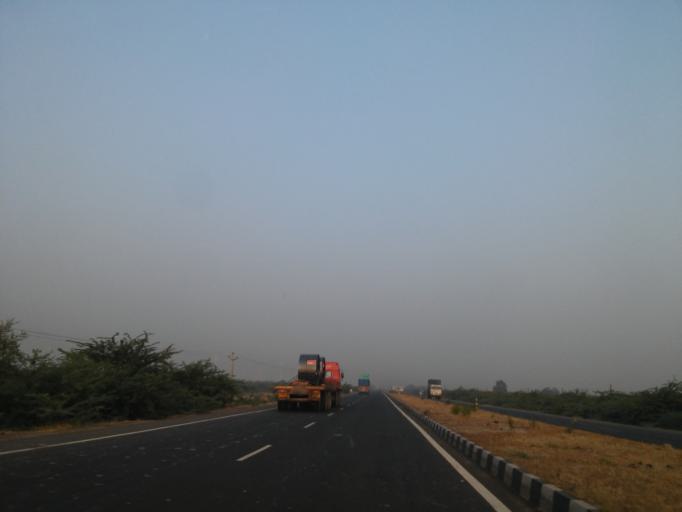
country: IN
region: Gujarat
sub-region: Kachchh
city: Rapar
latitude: 23.2255
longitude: 70.7039
